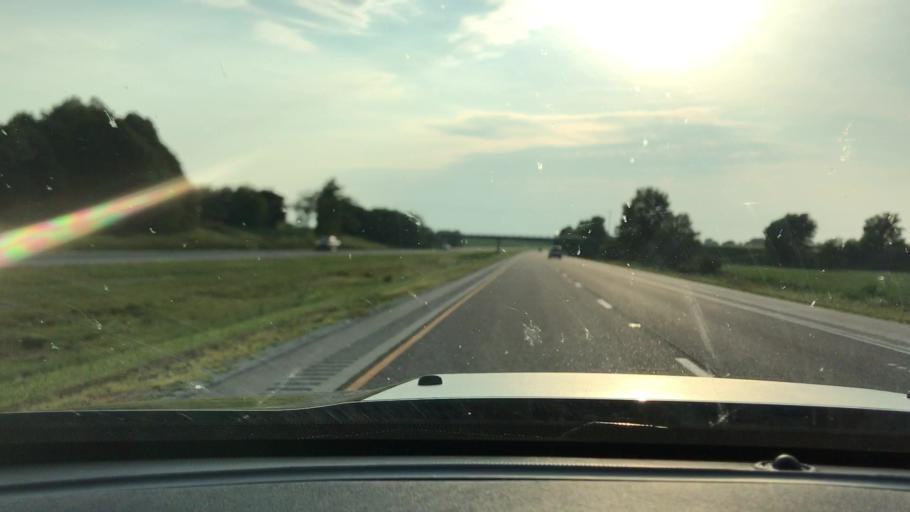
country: US
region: Illinois
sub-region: Henry County
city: Geneseo
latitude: 41.4155
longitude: -90.1212
